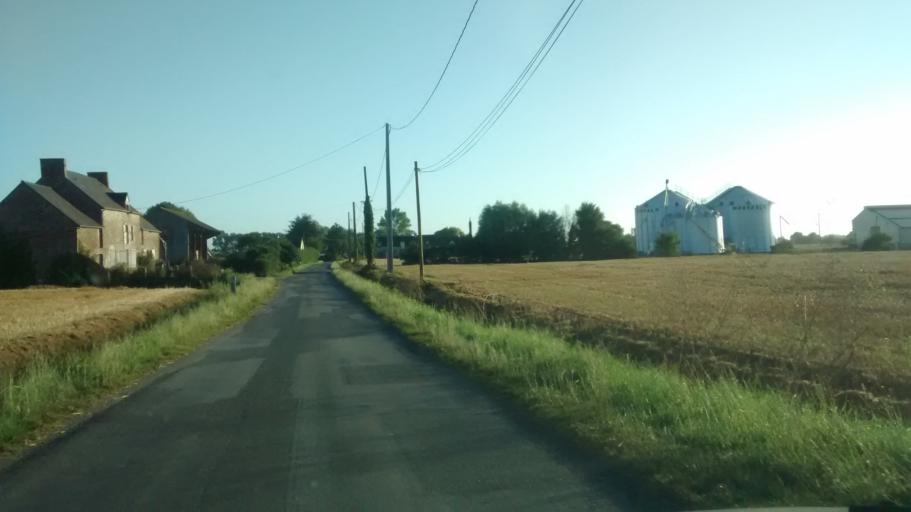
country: FR
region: Brittany
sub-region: Departement d'Ille-et-Vilaine
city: La Fresnais
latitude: 48.5986
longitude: -1.8543
